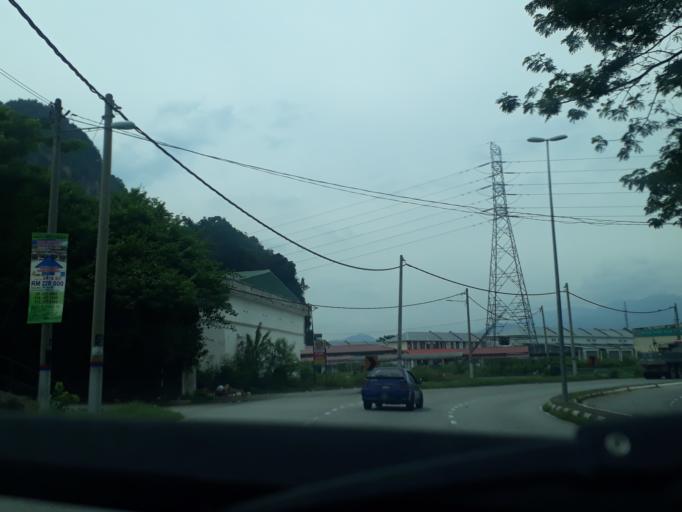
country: MY
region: Perak
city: Ipoh
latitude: 4.6414
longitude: 101.1553
